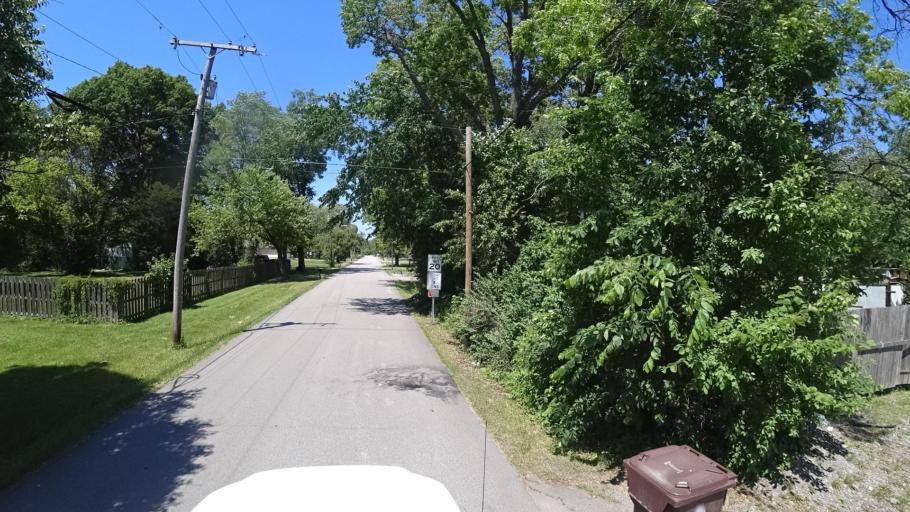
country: US
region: Indiana
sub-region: Porter County
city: Burns Harbor
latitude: 41.6006
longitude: -87.1394
